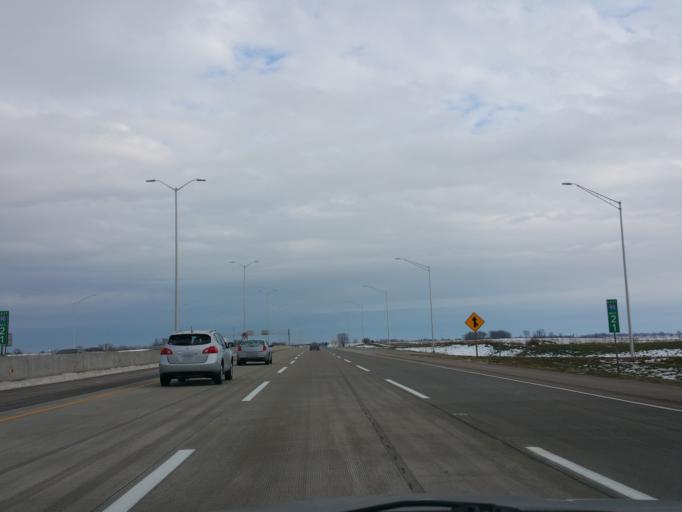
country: US
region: Illinois
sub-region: Winnebago County
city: Cherry Valley
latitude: 42.2330
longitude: -88.8971
